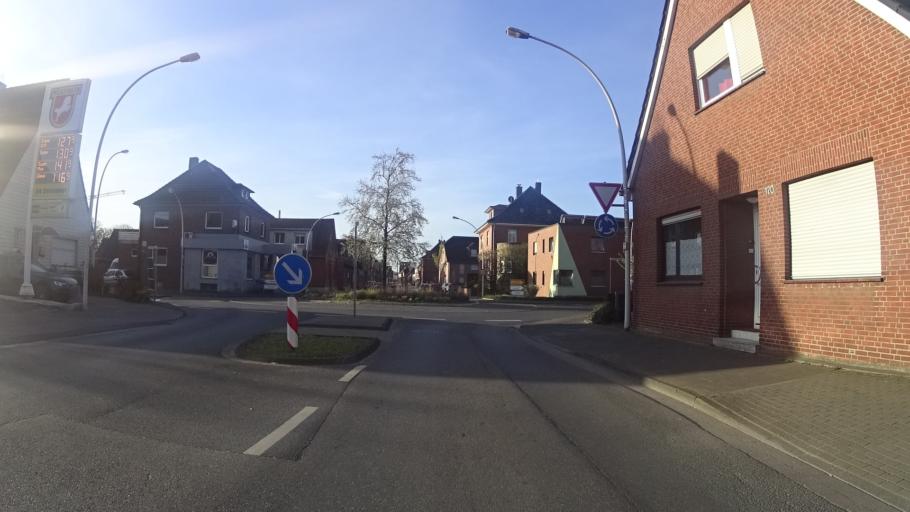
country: DE
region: North Rhine-Westphalia
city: Emsdetten
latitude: 52.1821
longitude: 7.5207
